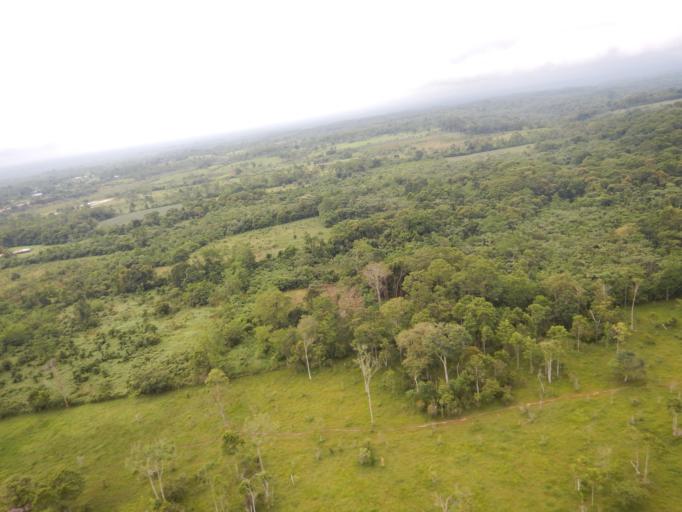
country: BO
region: Cochabamba
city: Chimore
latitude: -17.0743
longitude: -64.8953
